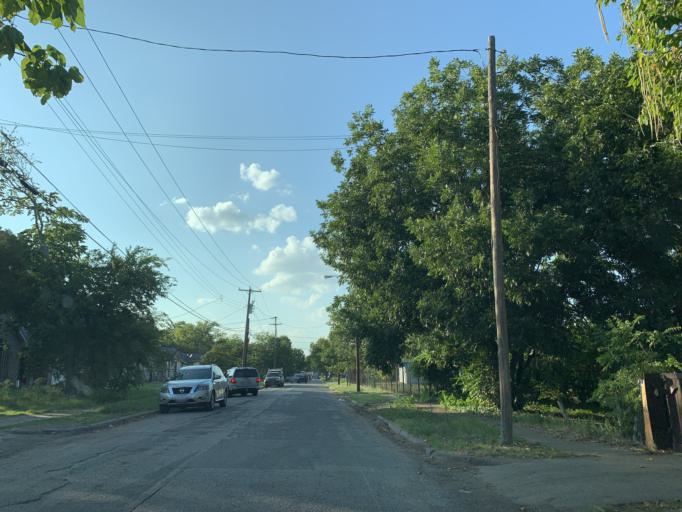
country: US
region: Texas
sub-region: Dallas County
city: Dallas
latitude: 32.6991
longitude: -96.7896
